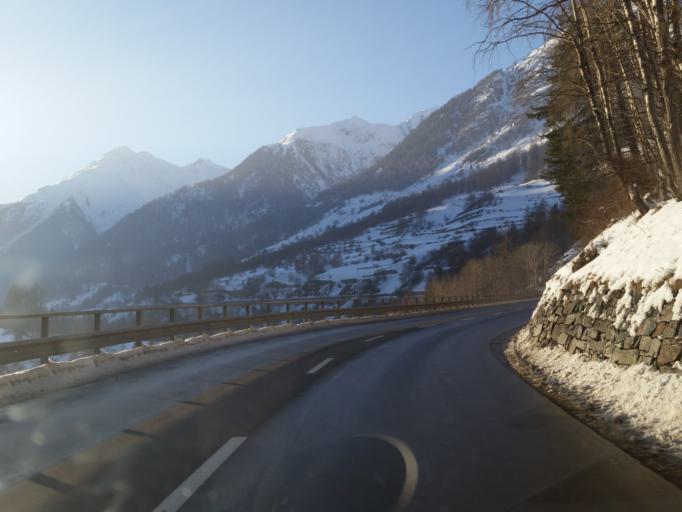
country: CH
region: Grisons
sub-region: Inn District
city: Zernez
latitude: 46.7704
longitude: 10.1405
